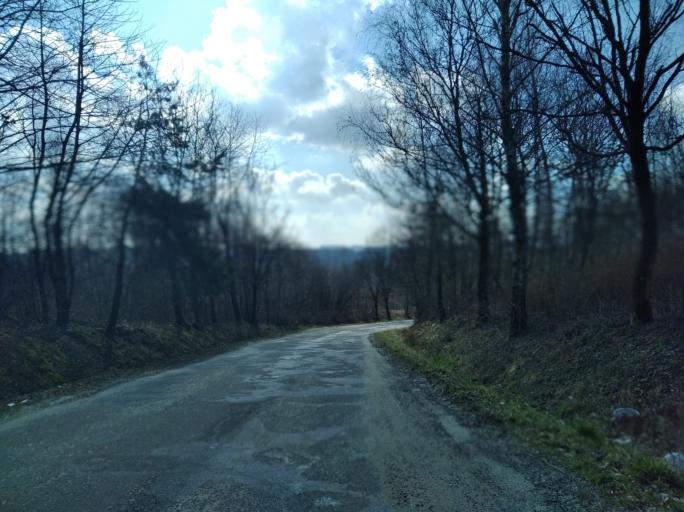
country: PL
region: Subcarpathian Voivodeship
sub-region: Powiat debicki
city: Brzostek
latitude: 49.8905
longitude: 21.4808
